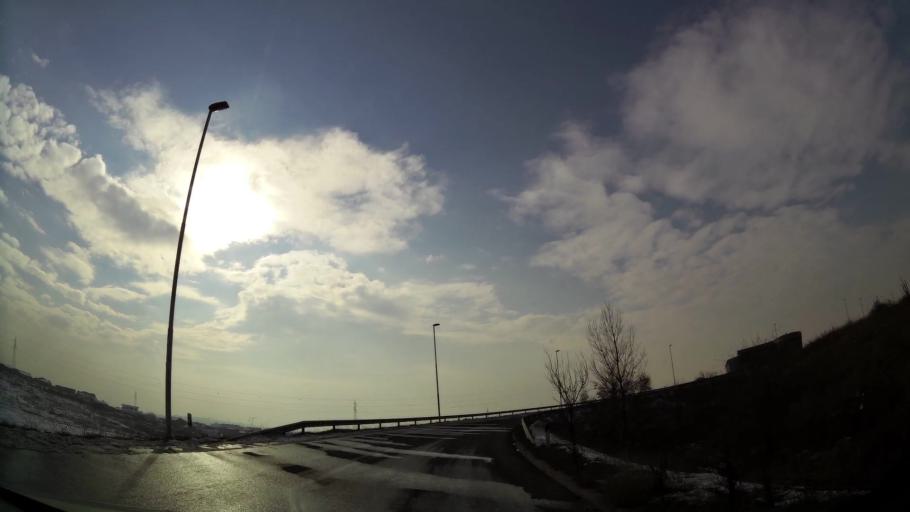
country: MK
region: Suto Orizari
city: Suto Orizare
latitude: 42.0516
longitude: 21.4223
